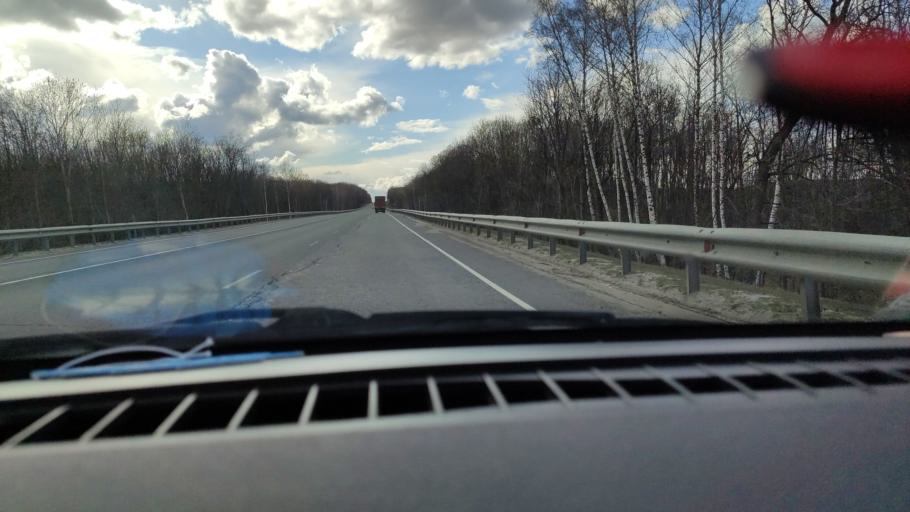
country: RU
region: Saratov
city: Vol'sk
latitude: 52.1070
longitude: 47.4172
